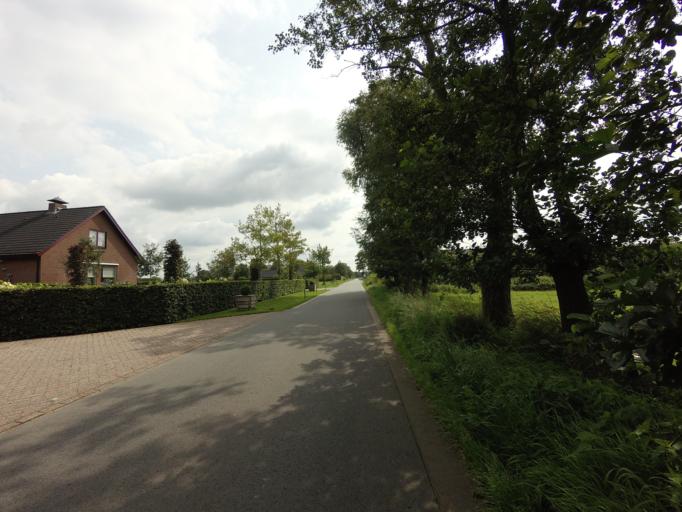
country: NL
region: Gelderland
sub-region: Gemeente Ede
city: Lunteren
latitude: 52.1107
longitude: 5.6146
